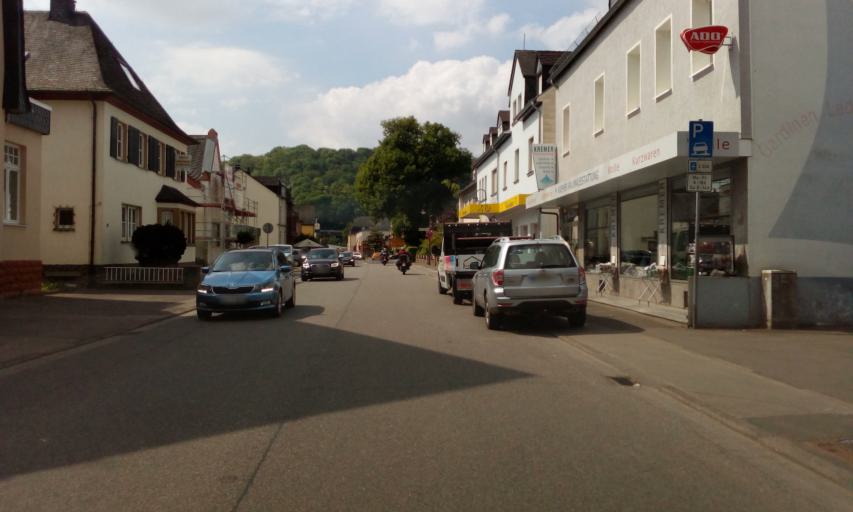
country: DE
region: Rheinland-Pfalz
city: Schweich
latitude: 49.8184
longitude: 6.7524
